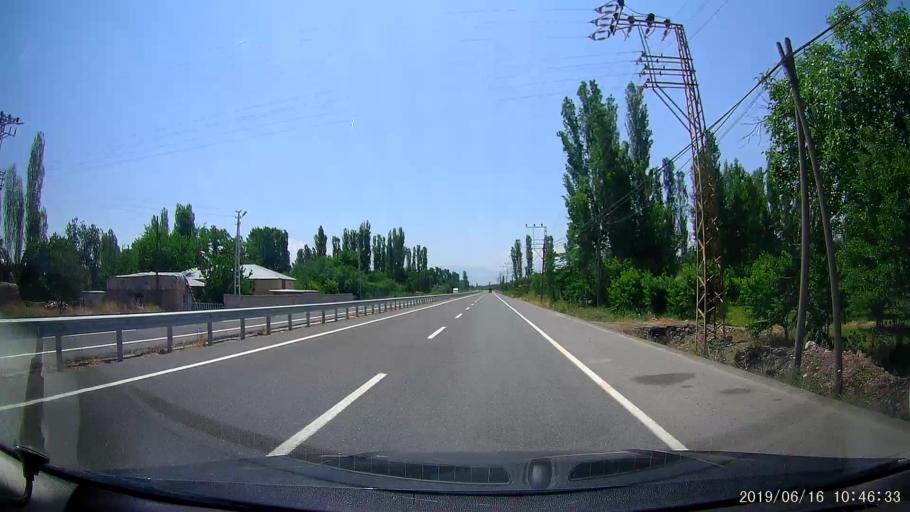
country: AM
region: Armavir
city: Shenavan
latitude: 40.0206
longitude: 43.8800
